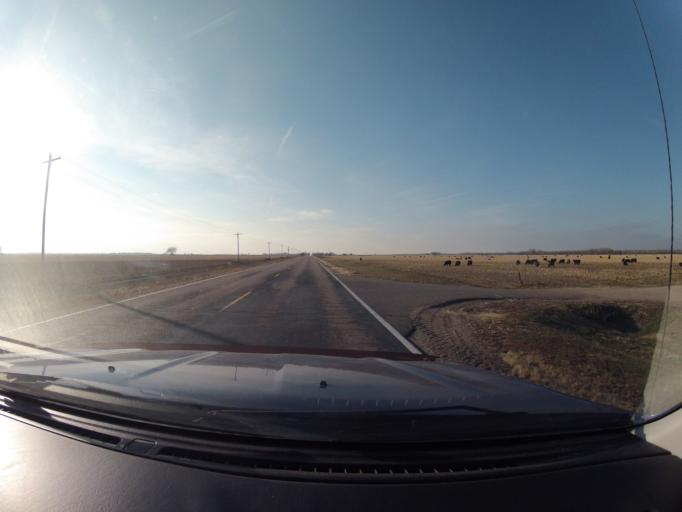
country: US
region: Nebraska
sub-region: Buffalo County
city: Kearney
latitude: 40.6410
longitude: -99.0571
